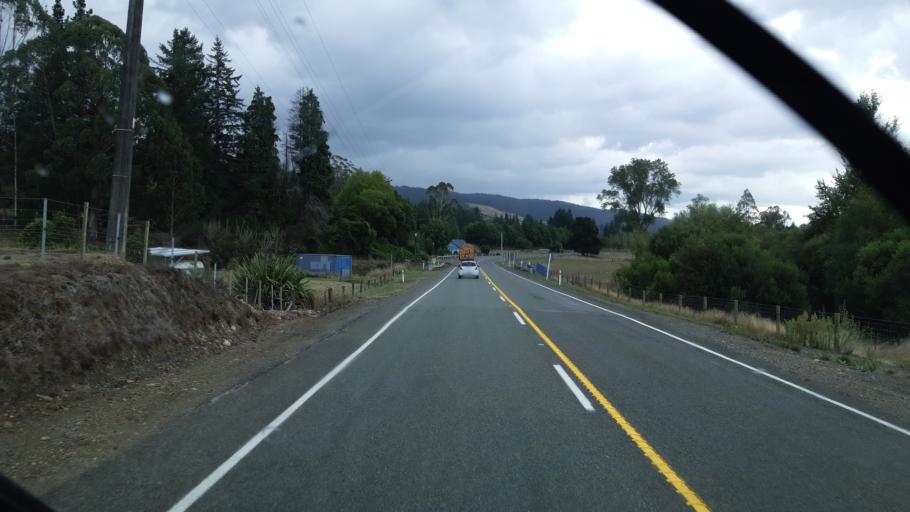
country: NZ
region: Tasman
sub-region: Tasman District
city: Wakefield
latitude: -41.4587
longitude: 172.9528
